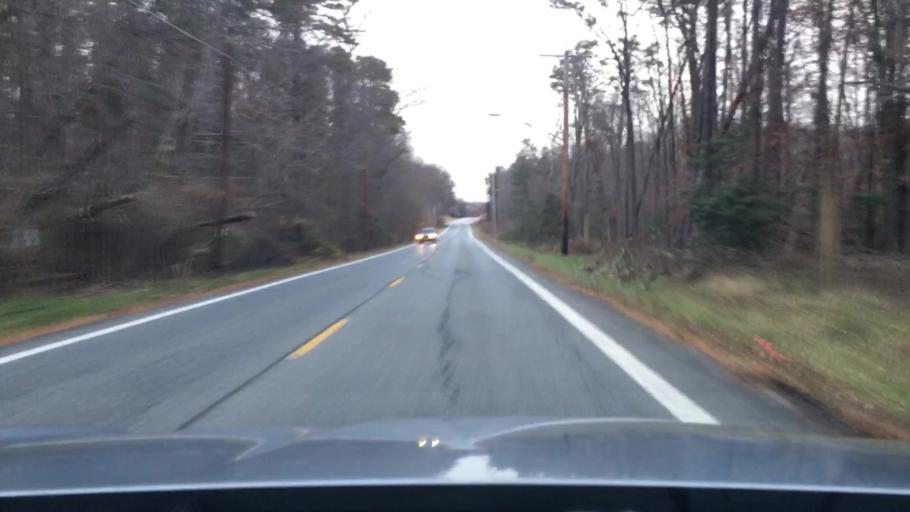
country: US
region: Maryland
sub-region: Prince George's County
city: Glenn Dale
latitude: 39.0269
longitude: -76.7856
